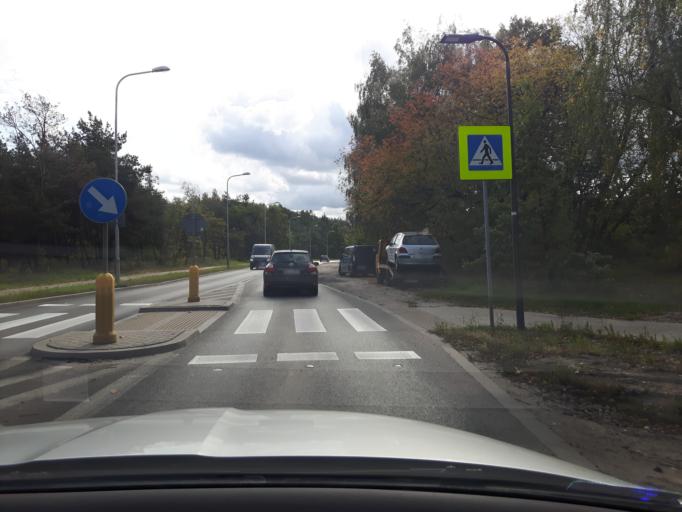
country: PL
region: Masovian Voivodeship
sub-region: Warszawa
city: Rembertow
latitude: 52.2355
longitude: 21.1431
